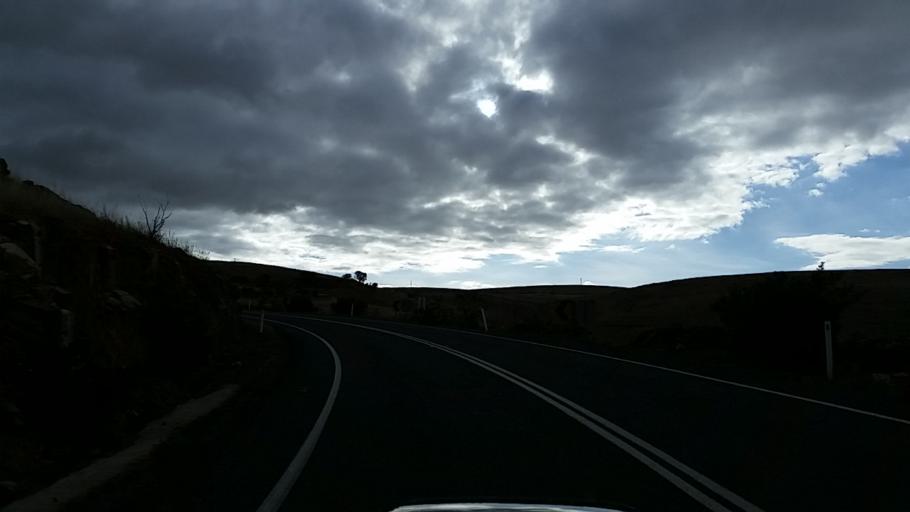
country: AU
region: South Australia
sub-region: Barossa
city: Angaston
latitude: -34.5617
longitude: 139.2173
